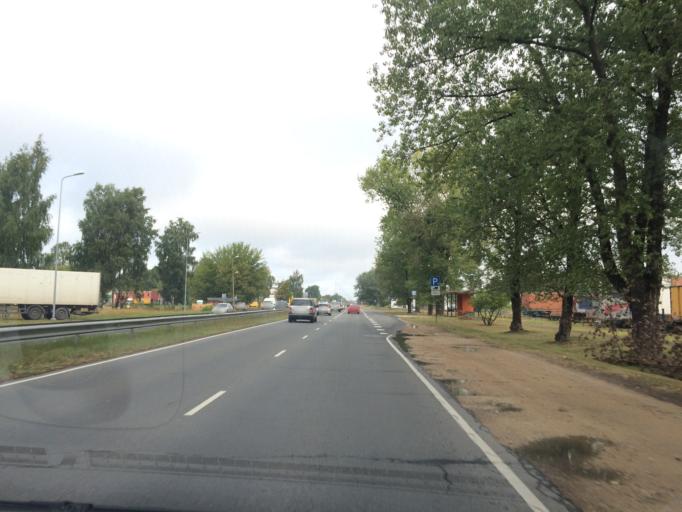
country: LV
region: Kekava
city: Kekava
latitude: 56.8880
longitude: 24.2323
